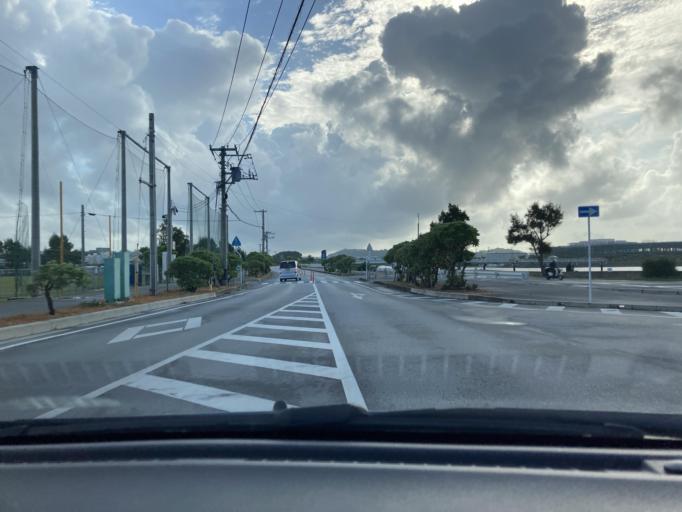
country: JP
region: Okinawa
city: Tomigusuku
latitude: 26.1750
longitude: 127.6451
